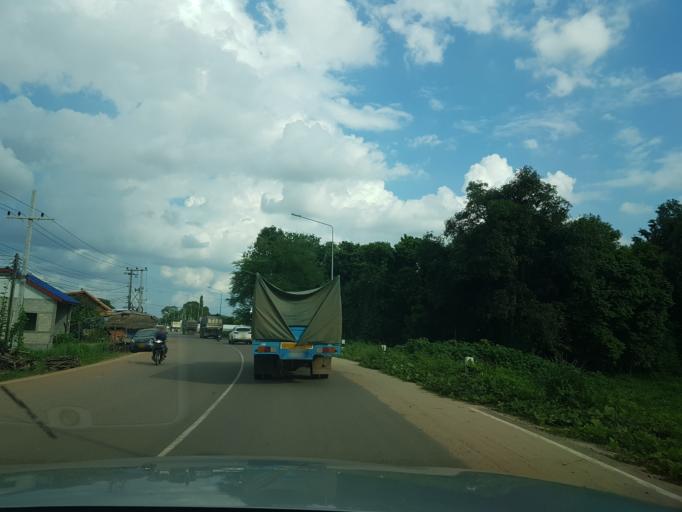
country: TH
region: Nong Khai
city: Si Chiang Mai
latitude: 17.9754
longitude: 102.4980
